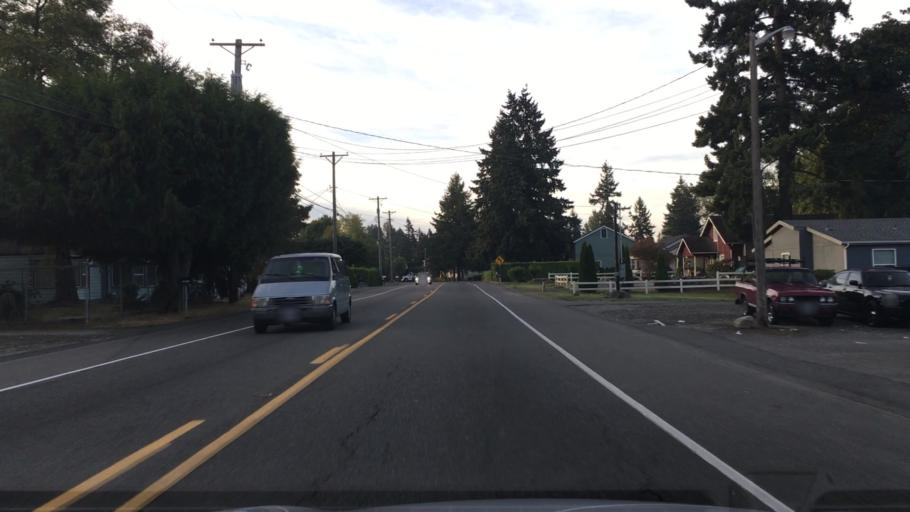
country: US
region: Washington
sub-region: Pierce County
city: Midland
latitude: 47.1787
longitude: -122.4078
